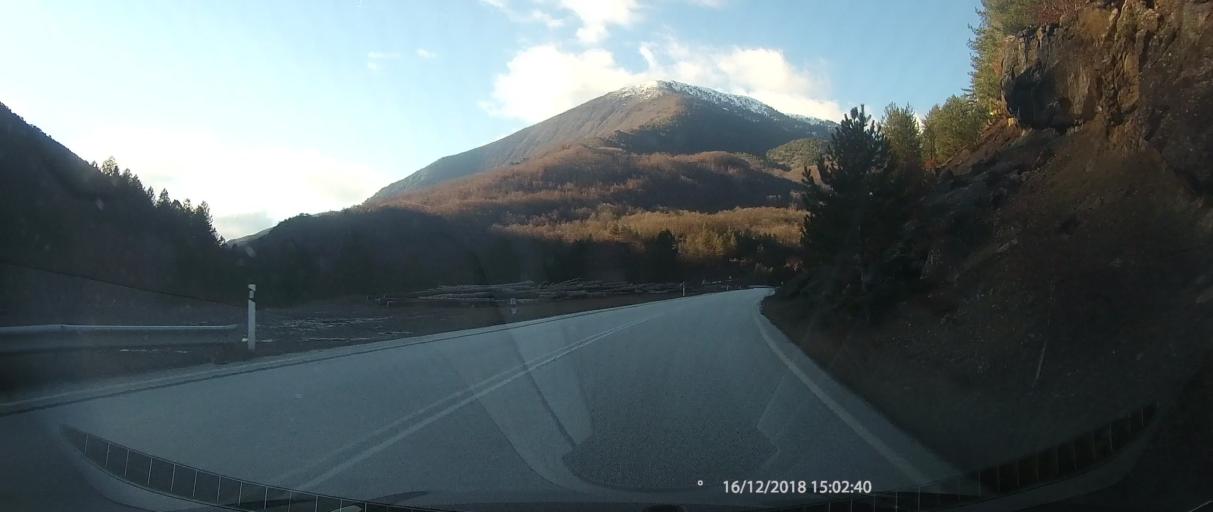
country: GR
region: West Macedonia
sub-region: Nomos Kastorias
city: Nestorio
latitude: 40.2293
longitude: 20.9922
